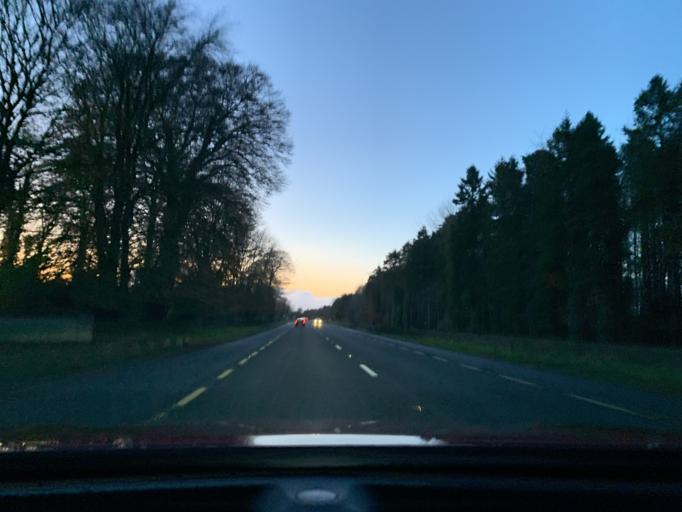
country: IE
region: Connaught
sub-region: Roscommon
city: Boyle
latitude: 53.9692
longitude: -8.2311
